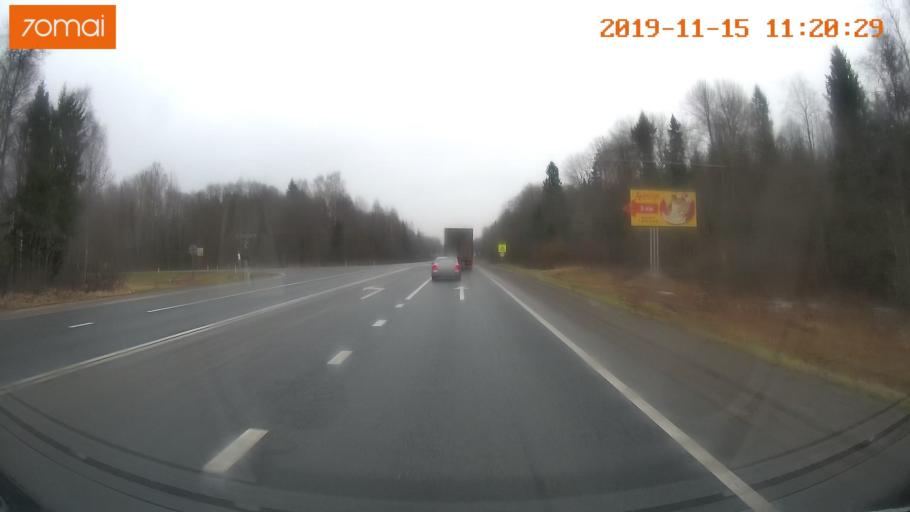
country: RU
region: Vologda
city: Molochnoye
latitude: 59.1417
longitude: 39.3163
